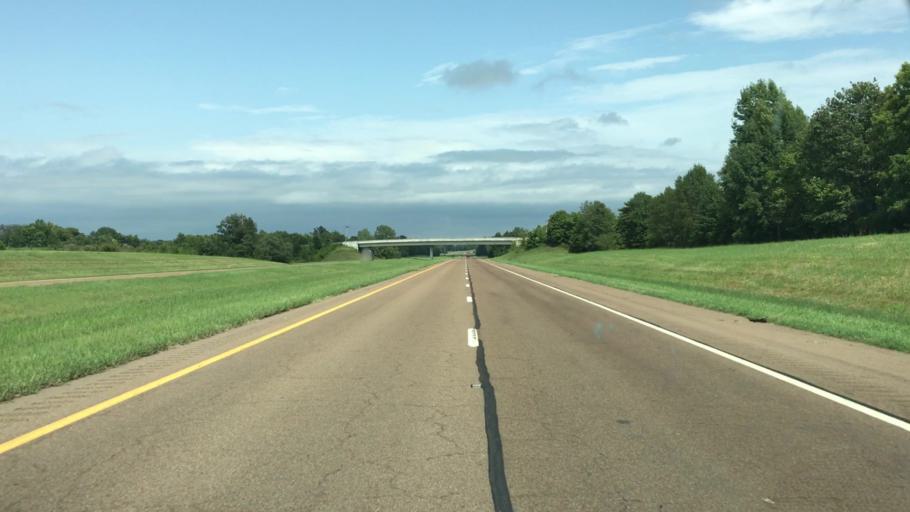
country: US
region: Tennessee
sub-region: Obion County
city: Union City
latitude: 36.4643
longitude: -88.9779
